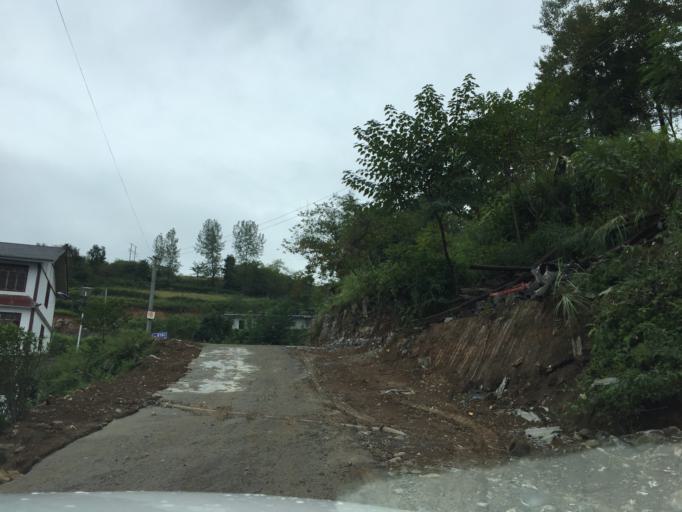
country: CN
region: Guizhou Sheng
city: Yantang
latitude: 28.2078
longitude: 108.0856
